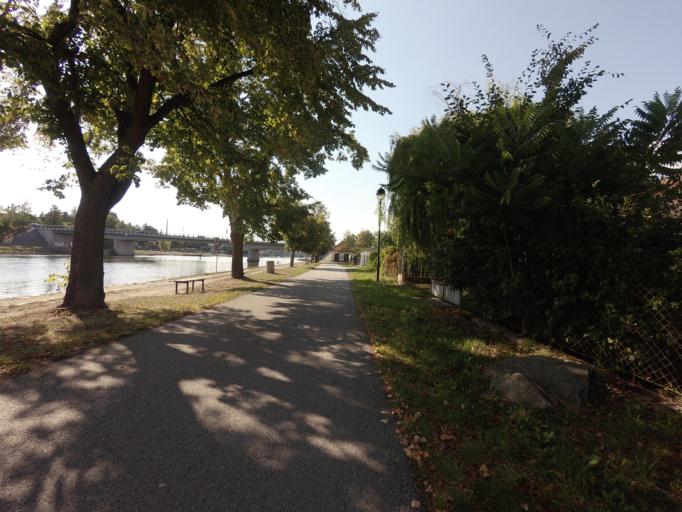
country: CZ
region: Jihocesky
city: Tyn nad Vltavou
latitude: 49.2211
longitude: 14.4231
